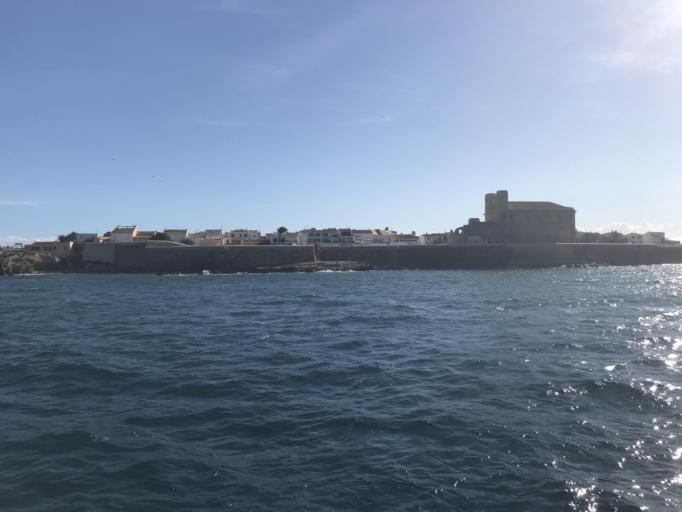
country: ES
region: Valencia
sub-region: Provincia de Alicante
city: Santa Pola
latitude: 38.1688
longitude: -0.4807
